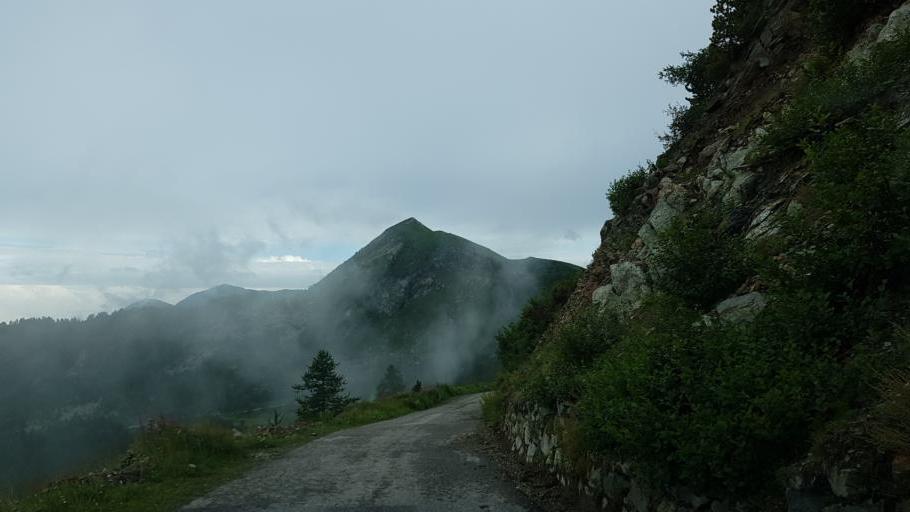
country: IT
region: Piedmont
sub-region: Provincia di Cuneo
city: Serre
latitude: 44.5517
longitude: 7.1252
